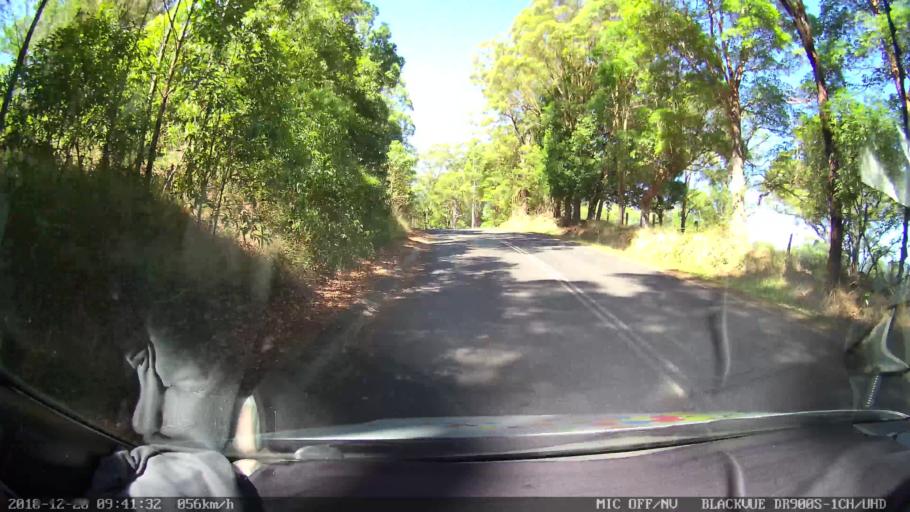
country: AU
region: New South Wales
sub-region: Lismore Municipality
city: Lismore
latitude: -28.7097
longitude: 153.2998
